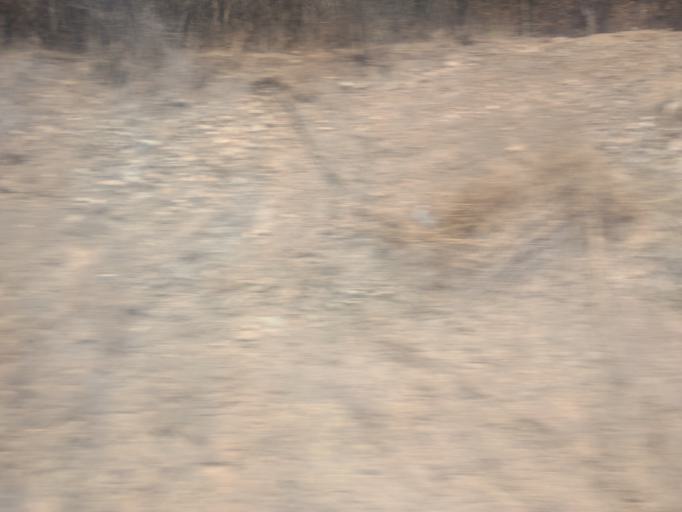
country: MX
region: Colima
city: El Colomo
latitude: 19.0523
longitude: -104.2688
